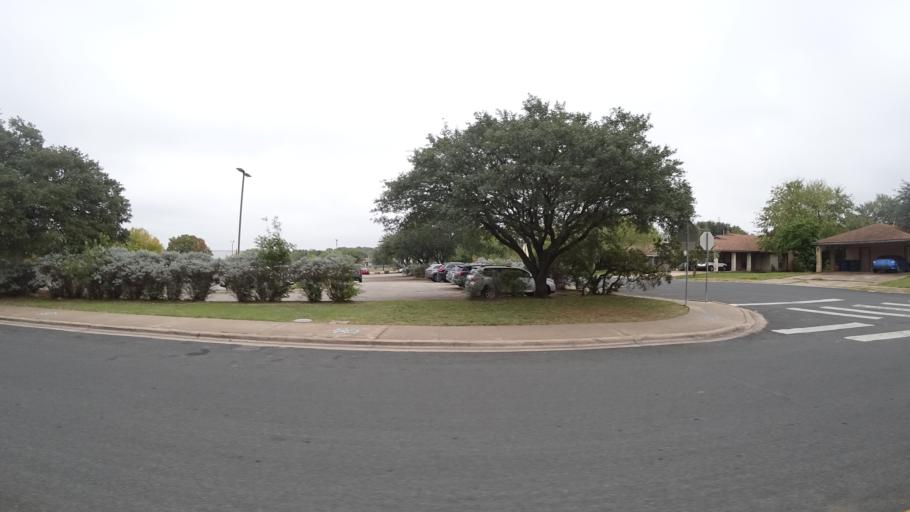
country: US
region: Texas
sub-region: Travis County
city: Shady Hollow
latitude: 30.2034
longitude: -97.8414
